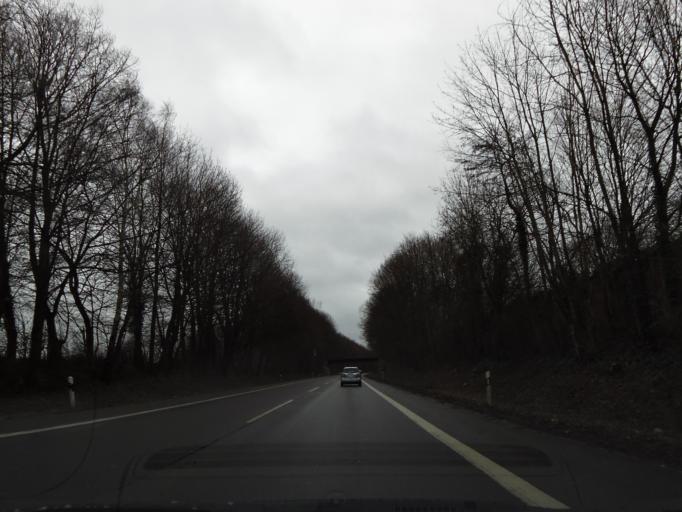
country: DE
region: North Rhine-Westphalia
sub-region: Regierungsbezirk Koln
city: Aachen
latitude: 50.8136
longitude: 6.0707
